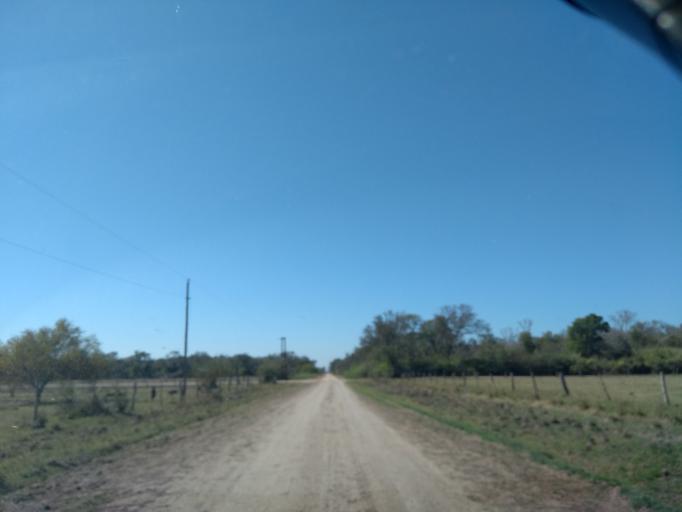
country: AR
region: Chaco
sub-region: Departamento de Quitilipi
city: Quitilipi
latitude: -26.7128
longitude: -60.2033
